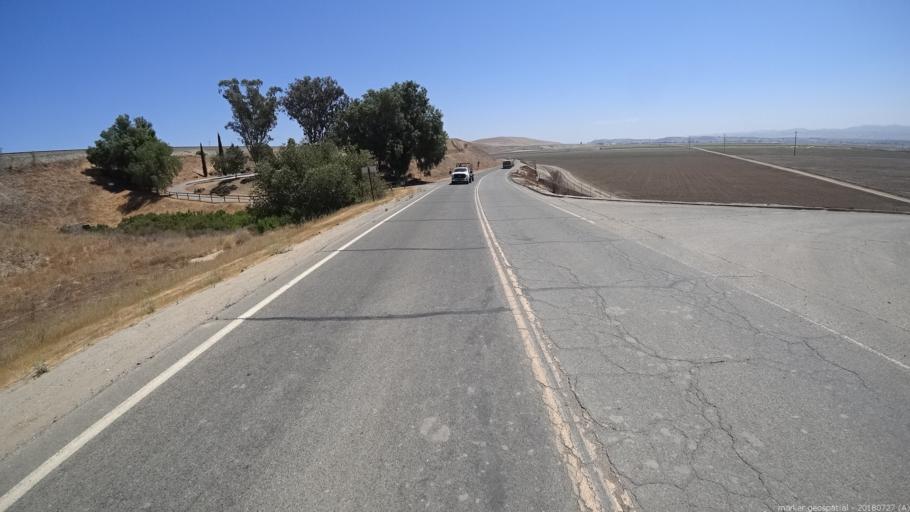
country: US
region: California
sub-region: Monterey County
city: King City
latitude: 36.1260
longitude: -121.0143
